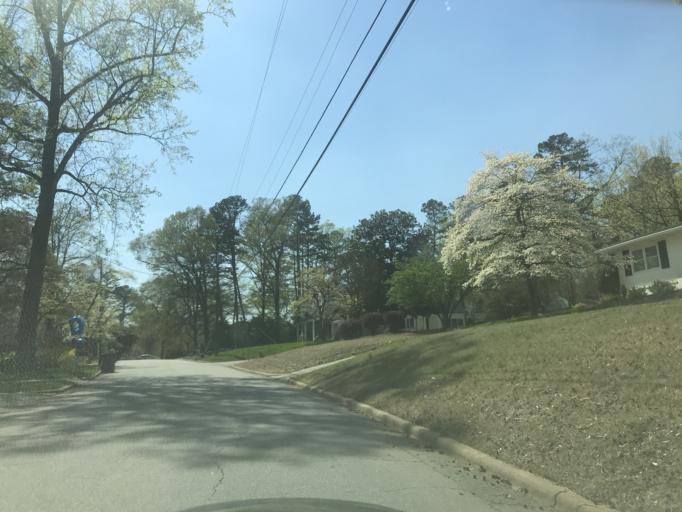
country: US
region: North Carolina
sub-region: Wake County
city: West Raleigh
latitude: 35.8245
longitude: -78.6399
